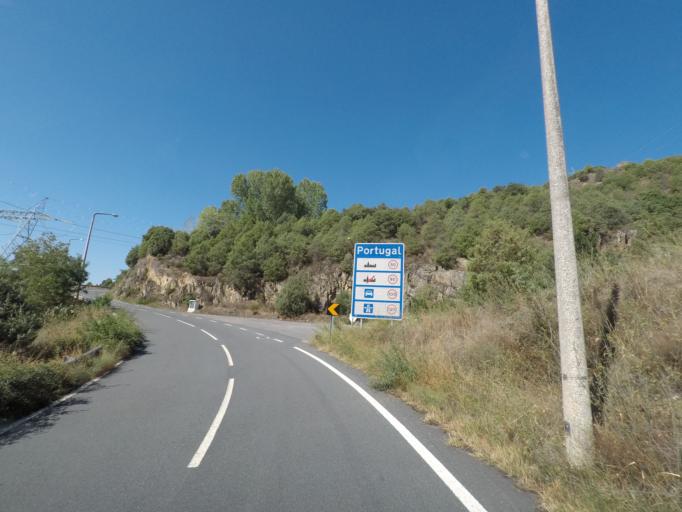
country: ES
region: Castille and Leon
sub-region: Provincia de Salamanca
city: Villarino de los Aires
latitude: 41.3011
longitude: -6.4748
